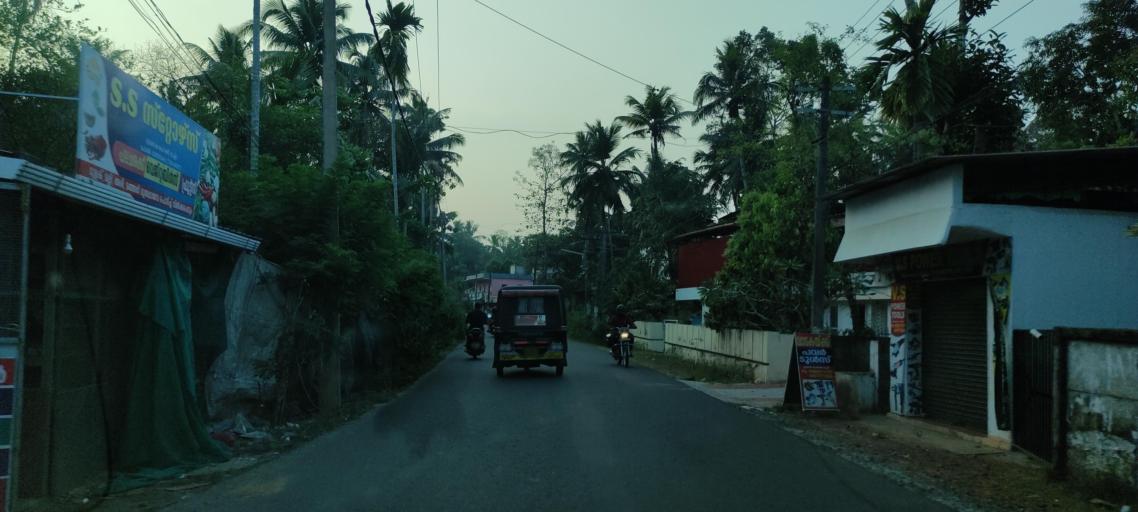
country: IN
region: Kerala
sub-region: Alappuzha
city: Kayankulam
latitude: 9.1376
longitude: 76.5161
